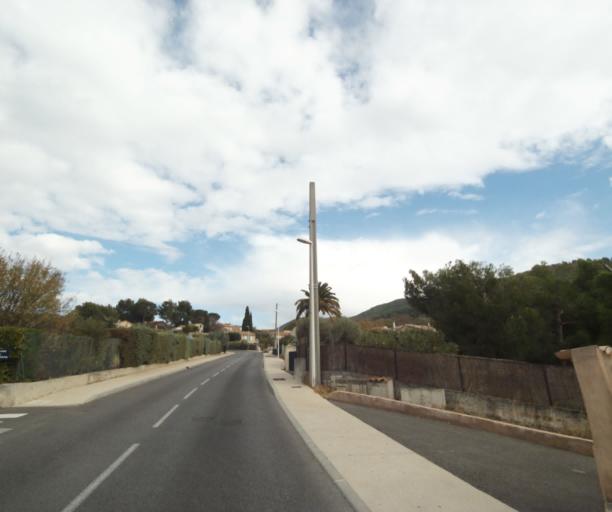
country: FR
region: Provence-Alpes-Cote d'Azur
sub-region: Departement des Bouches-du-Rhone
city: Ceyreste
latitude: 43.2164
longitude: 5.6340
